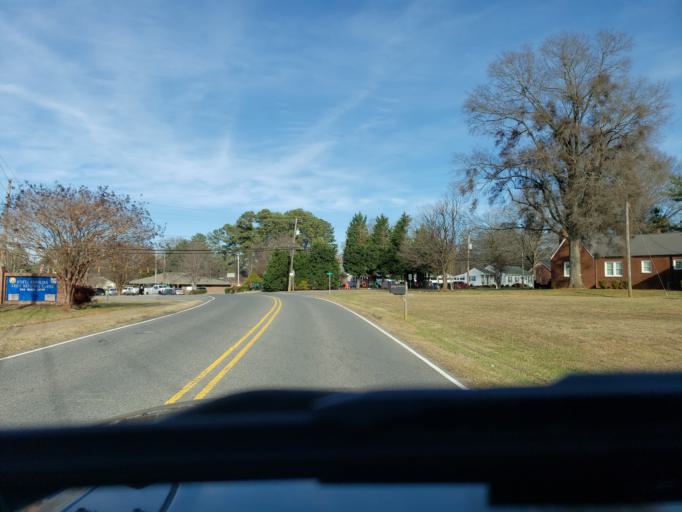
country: US
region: North Carolina
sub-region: Cleveland County
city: Kings Mountain
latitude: 35.2389
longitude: -81.3604
